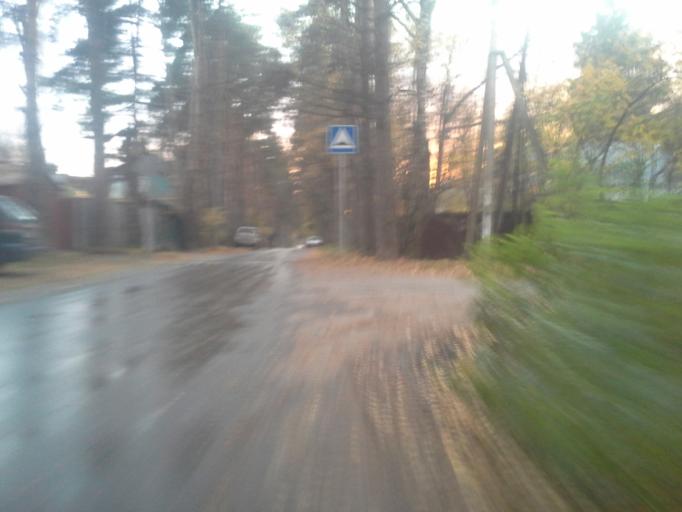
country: RU
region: Moskovskaya
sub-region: Leninskiy Rayon
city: Vnukovo
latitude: 55.6356
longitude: 37.2576
